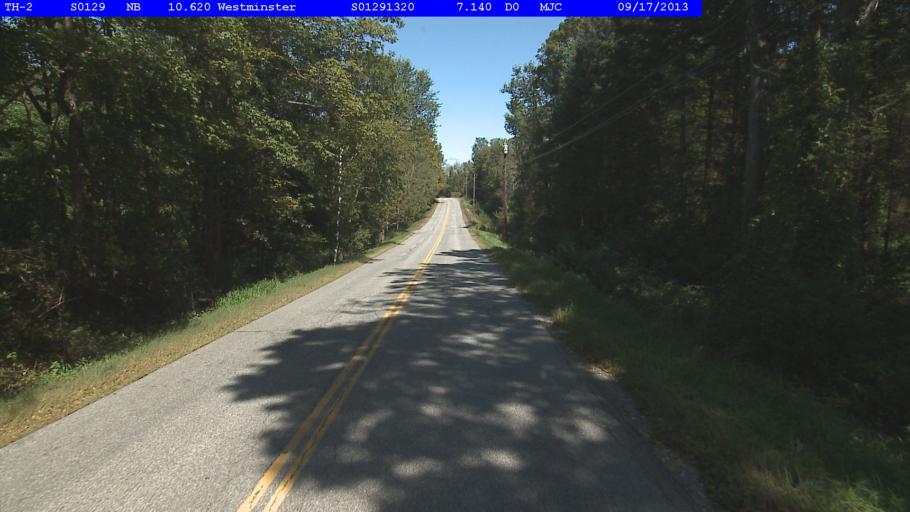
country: US
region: Vermont
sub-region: Windham County
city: Rockingham
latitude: 43.1169
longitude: -72.5345
